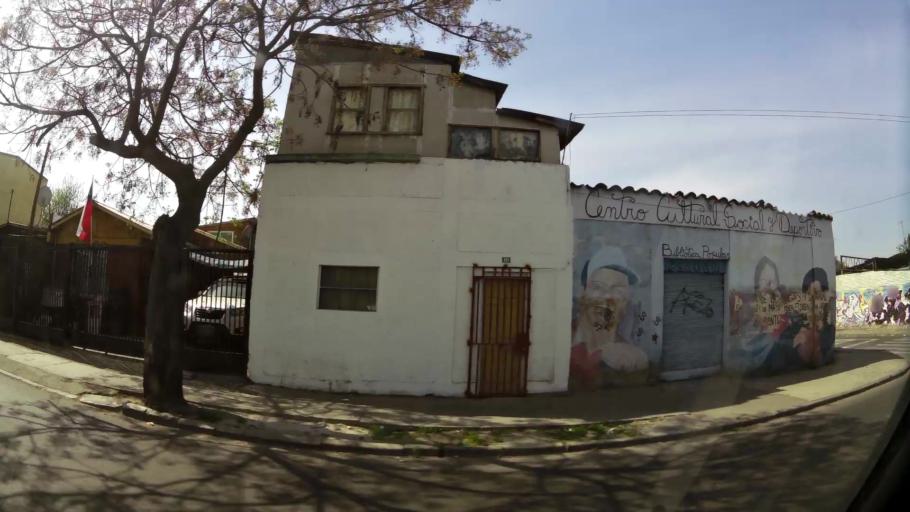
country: CL
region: Santiago Metropolitan
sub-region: Provincia de Santiago
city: Lo Prado
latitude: -33.4376
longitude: -70.7677
